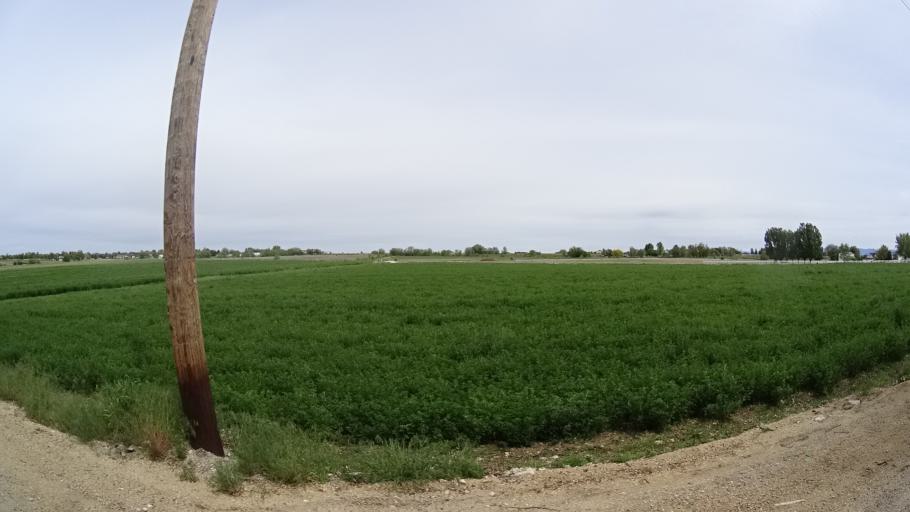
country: US
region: Idaho
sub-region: Ada County
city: Kuna
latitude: 43.5612
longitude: -116.4673
